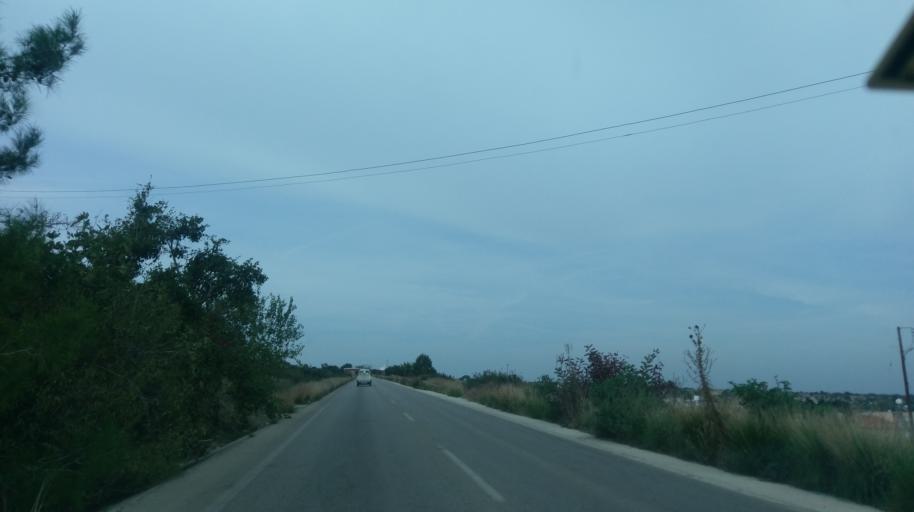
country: CY
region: Ammochostos
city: Leonarisso
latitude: 35.4258
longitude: 34.1269
